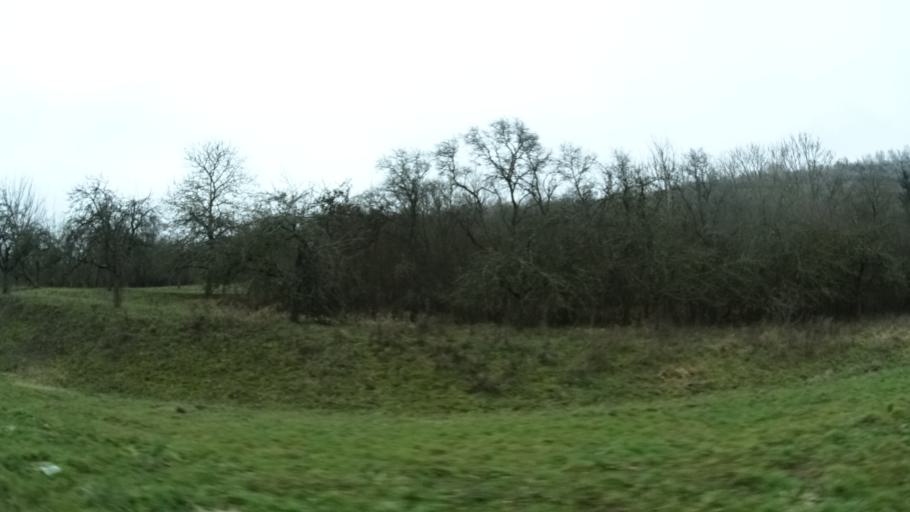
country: DE
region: Baden-Wuerttemberg
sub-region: Regierungsbezirk Stuttgart
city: Lauda-Konigshofen
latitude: 49.5387
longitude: 9.7213
